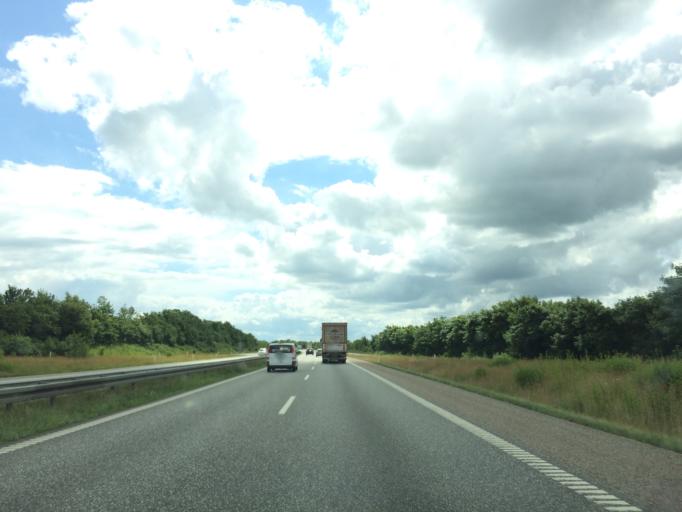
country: DK
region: North Denmark
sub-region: Mariagerfjord Kommune
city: Arden
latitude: 56.7810
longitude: 9.6965
